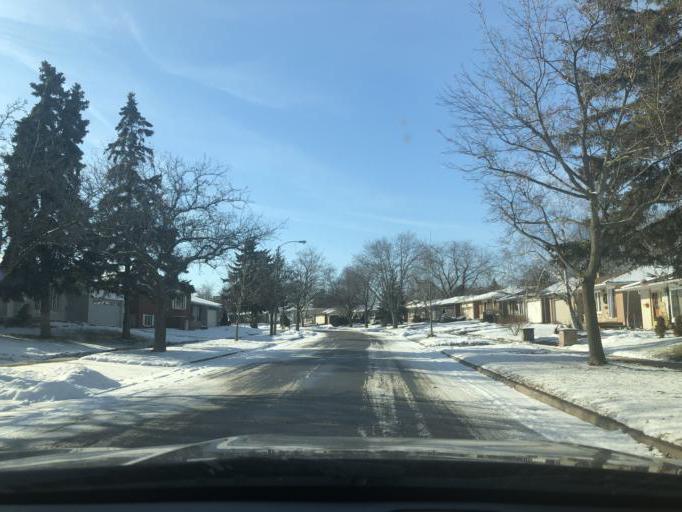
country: CA
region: Ontario
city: Pickering
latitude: 43.7841
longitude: -79.1409
